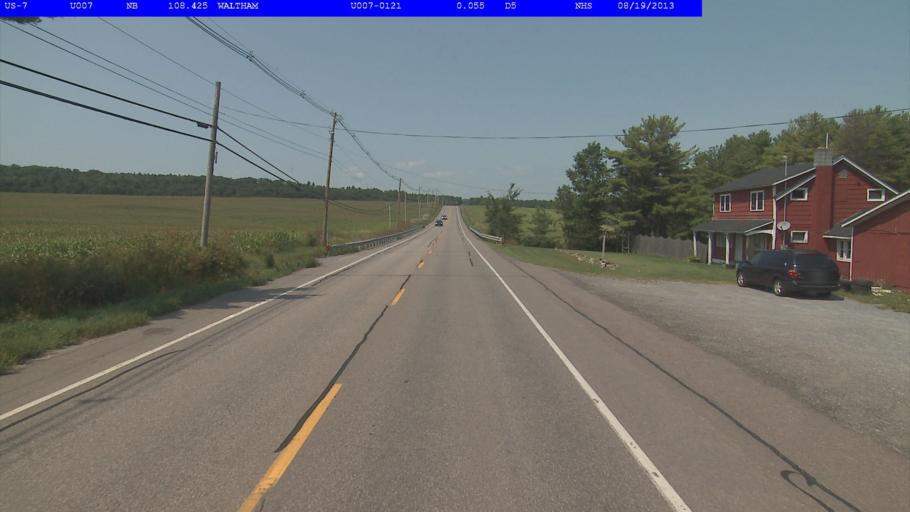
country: US
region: Vermont
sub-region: Addison County
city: Vergennes
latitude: 44.1482
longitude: -73.2109
